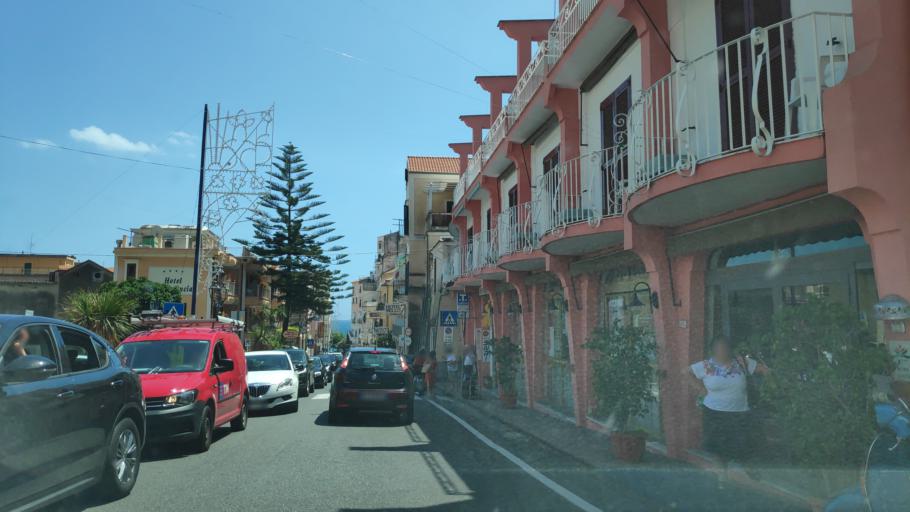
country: IT
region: Campania
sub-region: Provincia di Salerno
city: Minori
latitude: 40.6509
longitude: 14.6255
